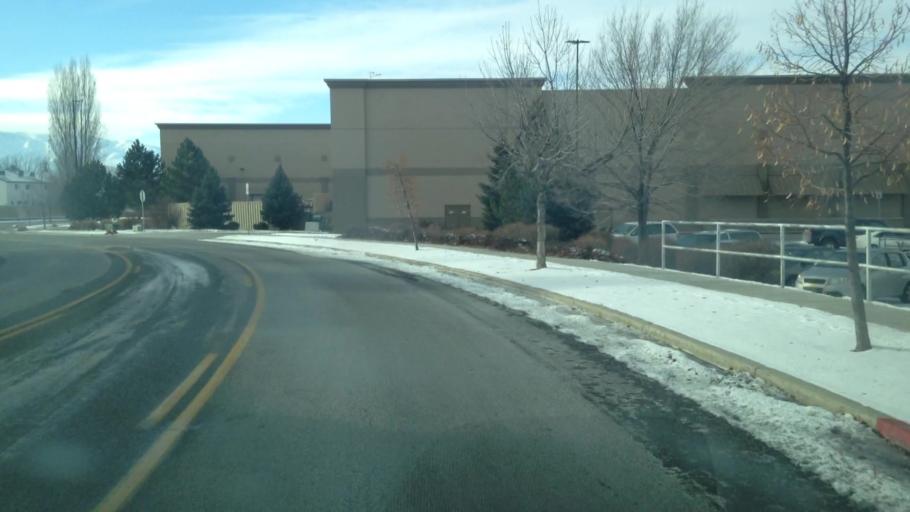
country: US
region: Utah
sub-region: Cache County
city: Logan
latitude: 41.7545
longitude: -111.8369
